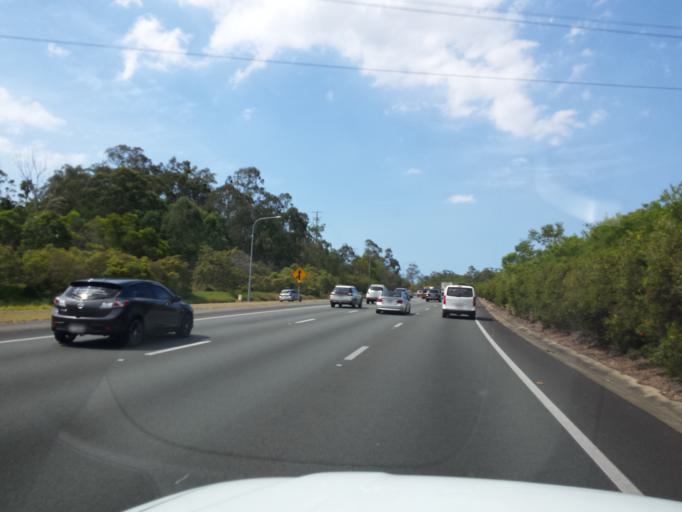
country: AU
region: Queensland
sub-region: Gold Coast
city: Nerang
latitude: -27.9777
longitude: 153.3436
